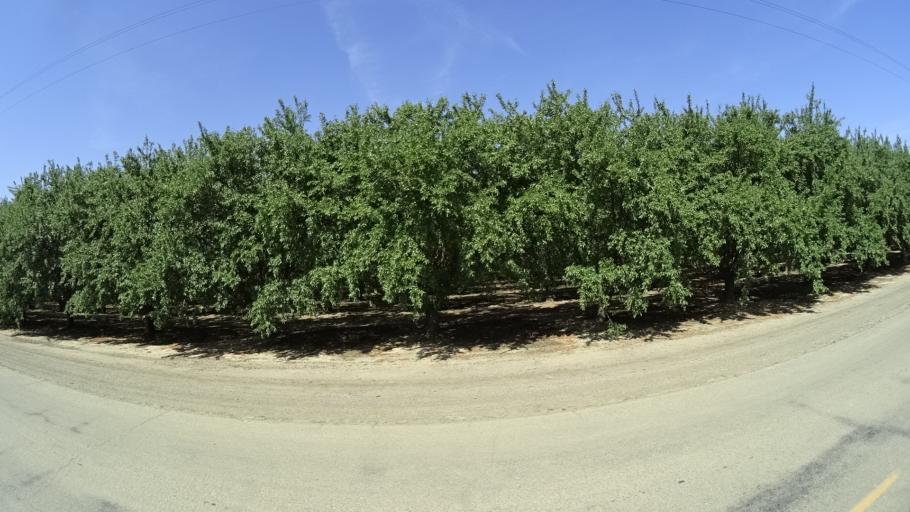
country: US
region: California
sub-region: Kings County
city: Kettleman City
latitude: 36.0902
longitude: -120.0037
